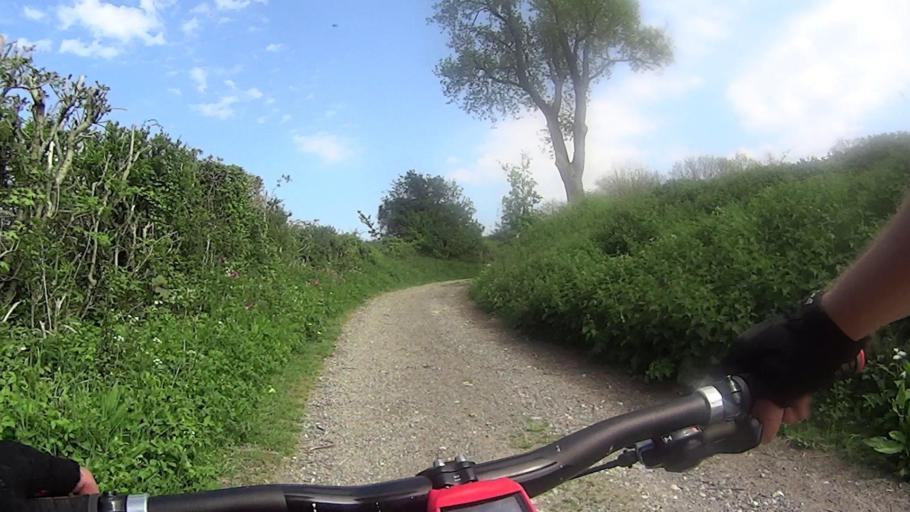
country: GB
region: England
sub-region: Hampshire
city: Petersfield
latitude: 50.9688
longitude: -0.9174
